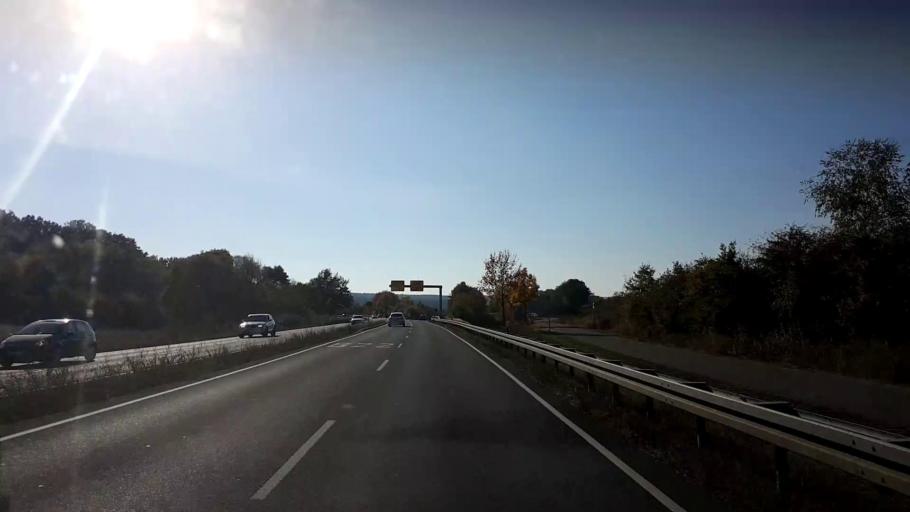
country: DE
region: Bavaria
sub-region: Upper Franconia
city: Stegaurach
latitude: 49.8682
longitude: 10.8635
